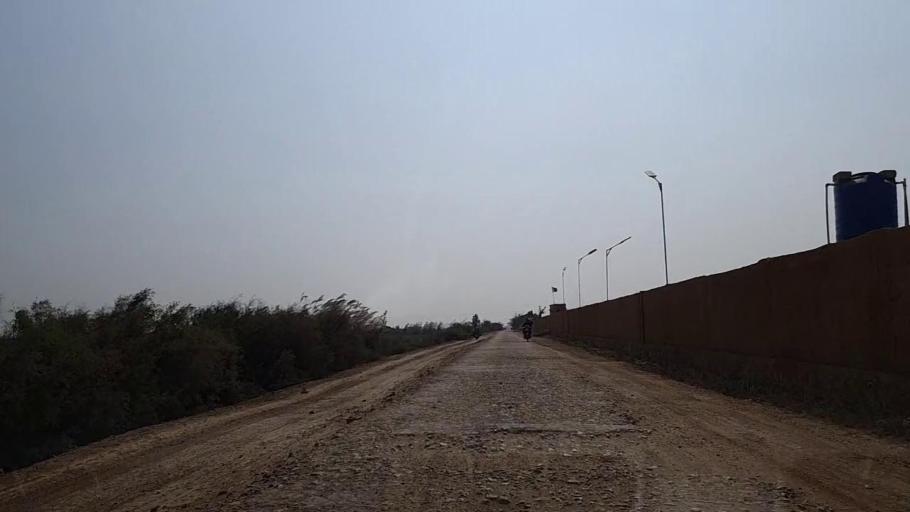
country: PK
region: Sindh
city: Thatta
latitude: 24.7086
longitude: 67.7674
